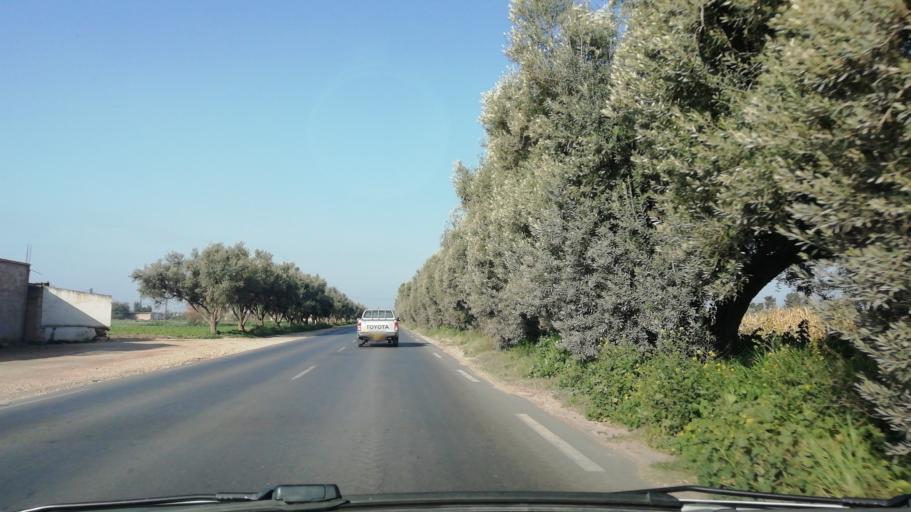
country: DZ
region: Mostaganem
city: Mostaganem
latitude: 35.7533
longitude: 0.1876
